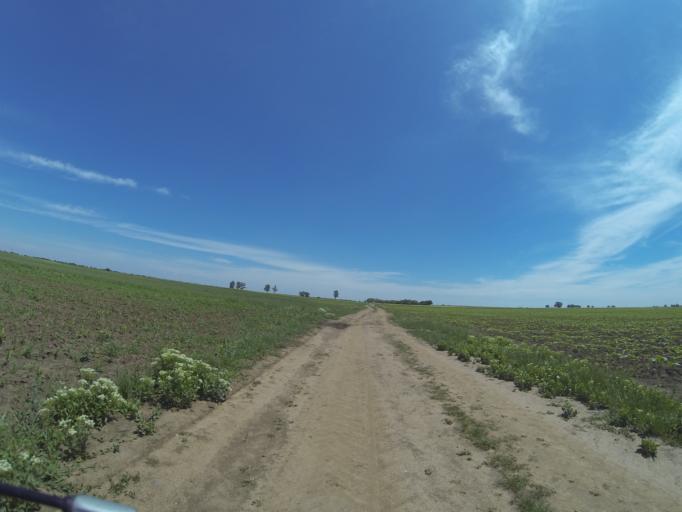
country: RO
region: Dolj
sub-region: Comuna Diosti
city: Radomir
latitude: 44.1466
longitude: 24.1572
